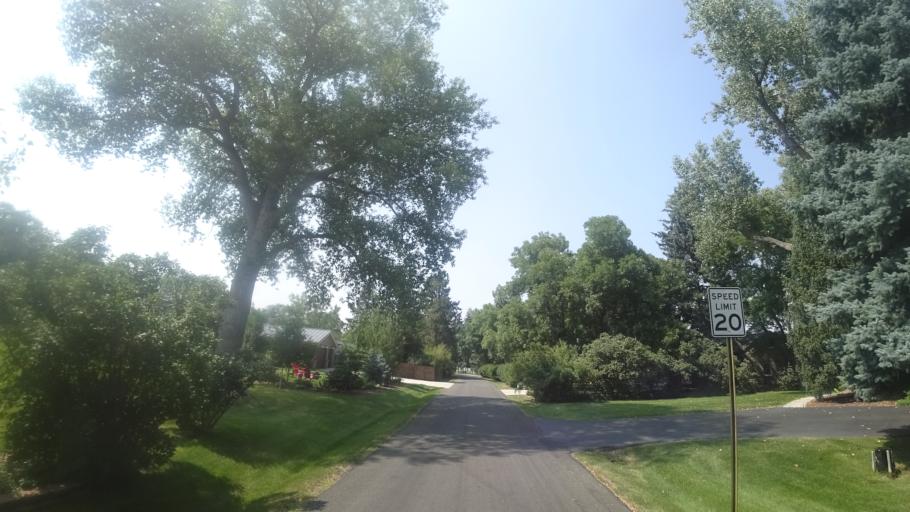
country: US
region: Colorado
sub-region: Arapahoe County
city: Cherry Hills Village
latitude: 39.6270
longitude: -104.9751
